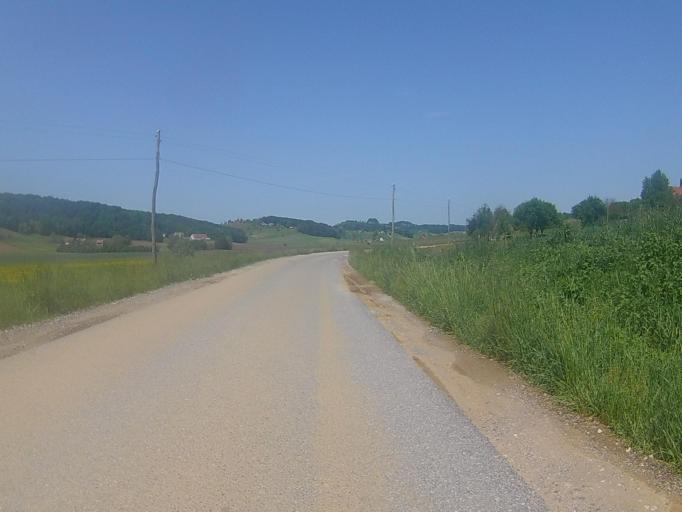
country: SI
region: Sveti Jurij v Slovenskih Goricah
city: Jurovski Dol
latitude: 46.5806
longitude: 15.7532
